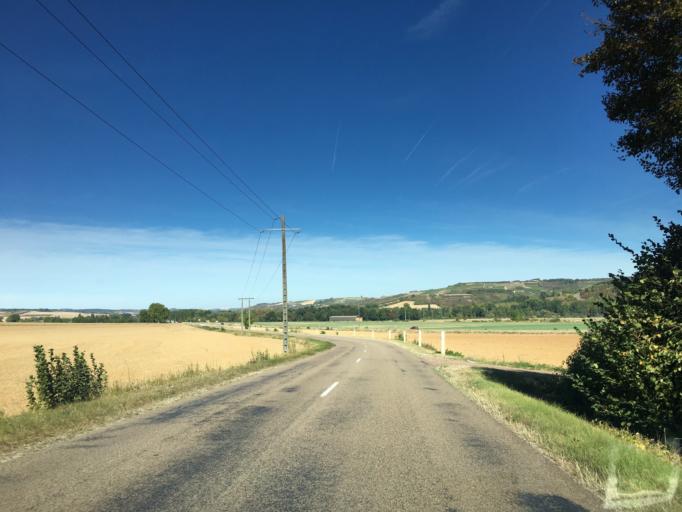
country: FR
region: Bourgogne
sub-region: Departement de l'Yonne
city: Saint-Bris-le-Vineux
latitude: 47.6872
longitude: 3.6522
